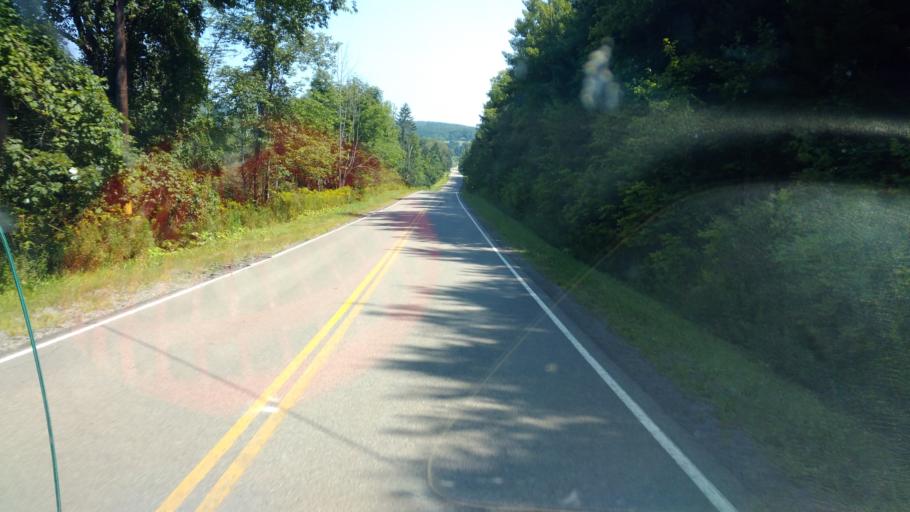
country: US
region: New York
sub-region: Allegany County
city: Alfred
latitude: 42.2975
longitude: -77.8946
